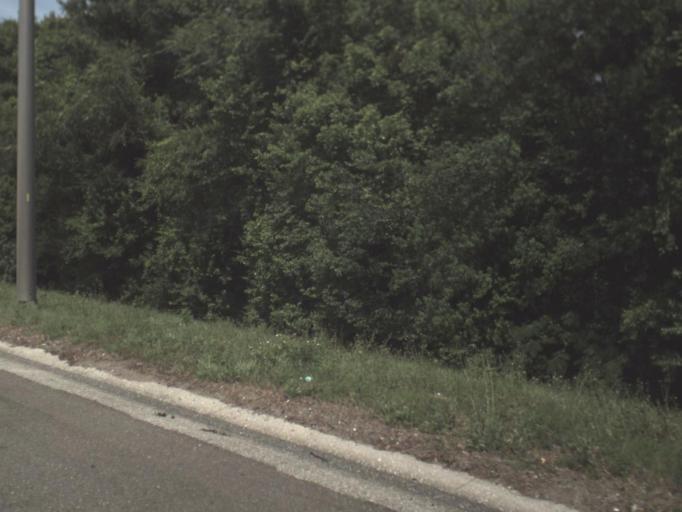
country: US
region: Florida
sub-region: Duval County
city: Jacksonville
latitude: 30.3491
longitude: -81.7607
